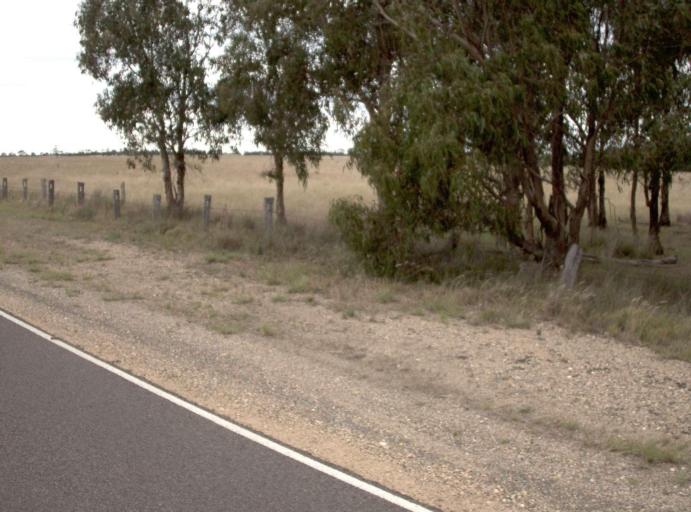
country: AU
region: Victoria
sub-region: East Gippsland
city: Bairnsdale
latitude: -37.9647
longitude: 147.4862
